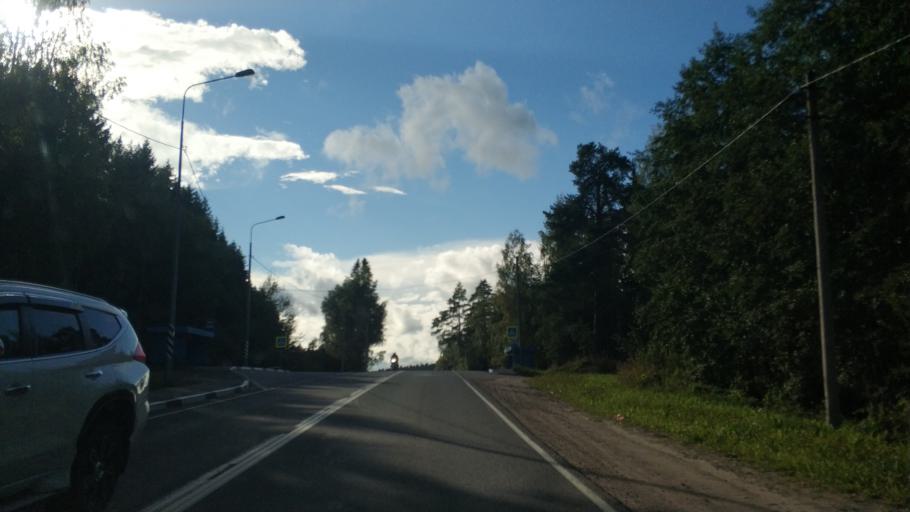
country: RU
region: Republic of Karelia
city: Lakhdenpokh'ya
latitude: 61.5232
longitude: 30.1682
